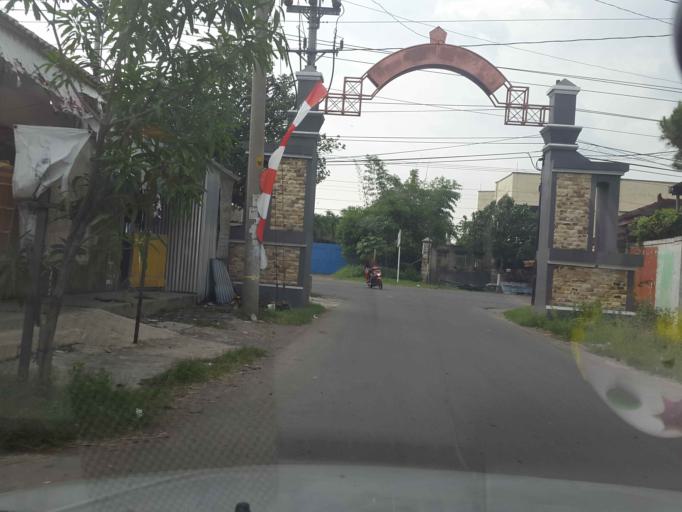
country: ID
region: Central Java
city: Jaten
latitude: -7.5506
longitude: 110.8889
